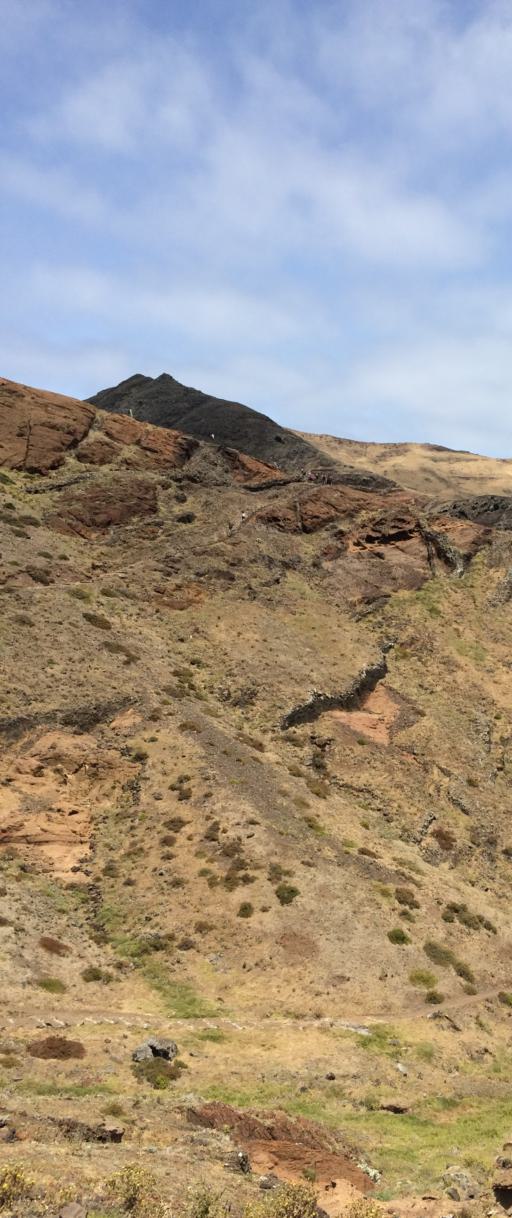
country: PT
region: Madeira
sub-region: Machico
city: Canical
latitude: 32.7481
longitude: -16.6979
